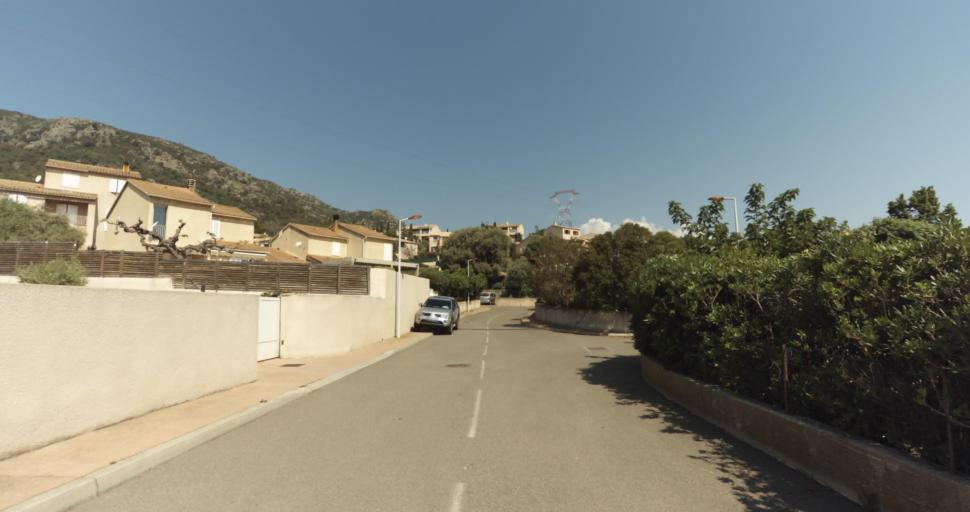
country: FR
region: Corsica
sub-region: Departement de la Haute-Corse
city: Biguglia
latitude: 42.6194
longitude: 9.4251
